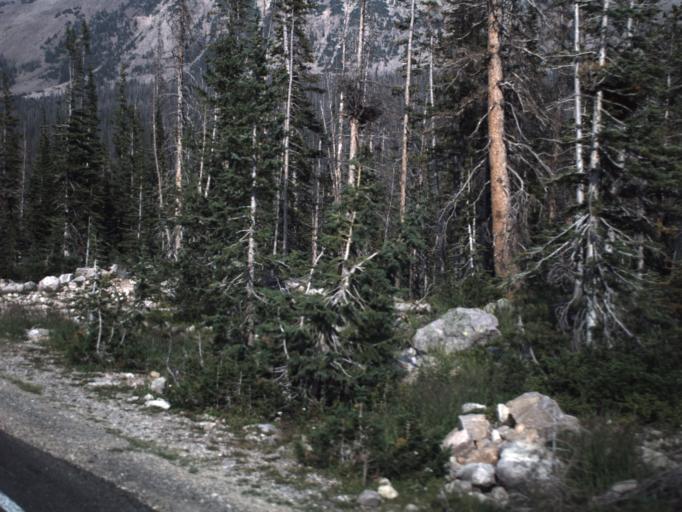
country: US
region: Utah
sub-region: Summit County
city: Kamas
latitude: 40.7334
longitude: -110.8676
